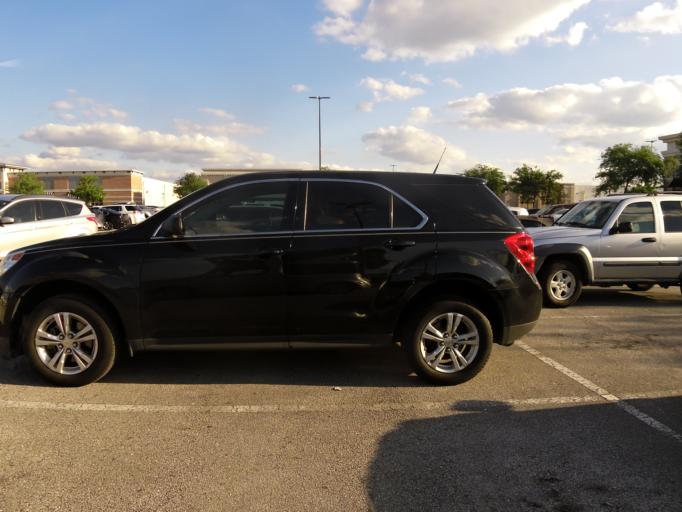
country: US
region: Florida
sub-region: Duval County
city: Jacksonville Beach
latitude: 30.2597
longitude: -81.5269
